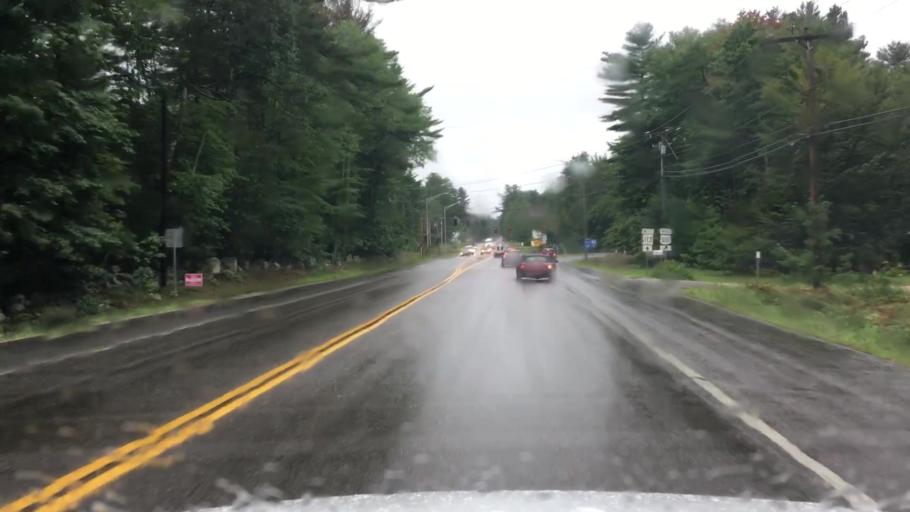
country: US
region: New Hampshire
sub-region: Carroll County
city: Conway
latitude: 43.9939
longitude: -71.0815
